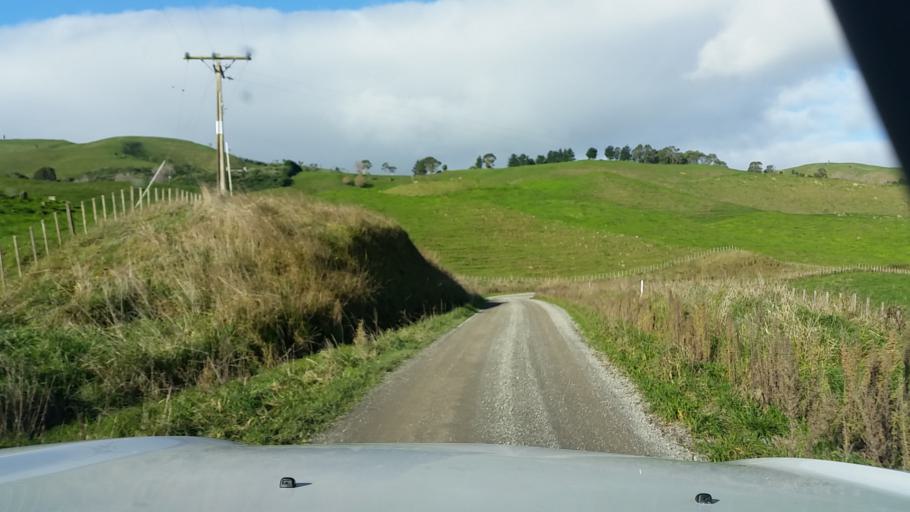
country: NZ
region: Wellington
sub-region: Masterton District
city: Masterton
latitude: -41.0472
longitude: 175.6943
